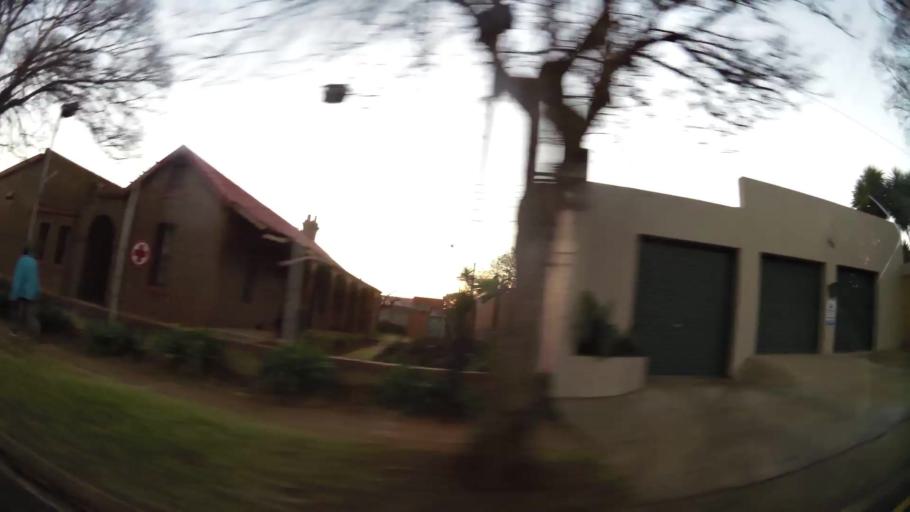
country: ZA
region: Gauteng
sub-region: City of Johannesburg Metropolitan Municipality
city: Roodepoort
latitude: -26.1736
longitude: 27.9183
